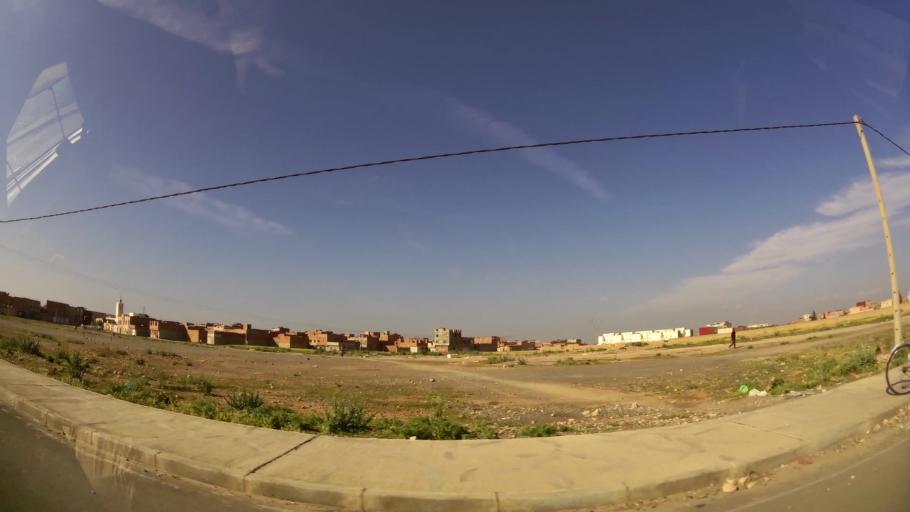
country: MA
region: Oriental
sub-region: Oujda-Angad
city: Oujda
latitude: 34.7210
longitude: -1.8906
